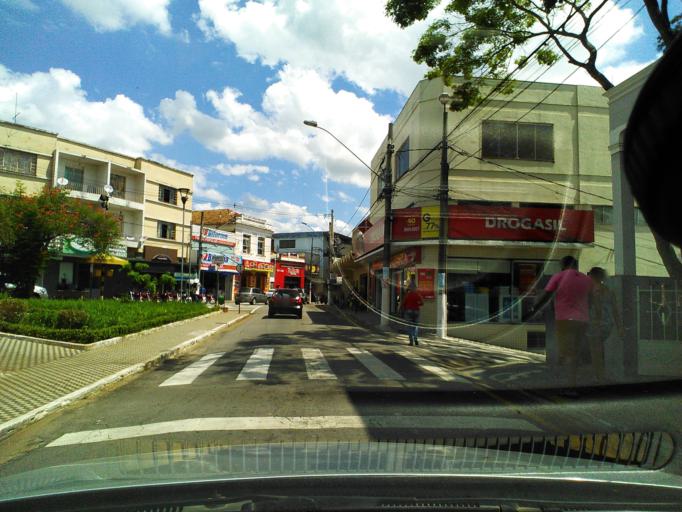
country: BR
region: Minas Gerais
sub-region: Tres Coracoes
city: Tres Coracoes
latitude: -21.6974
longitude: -45.2563
